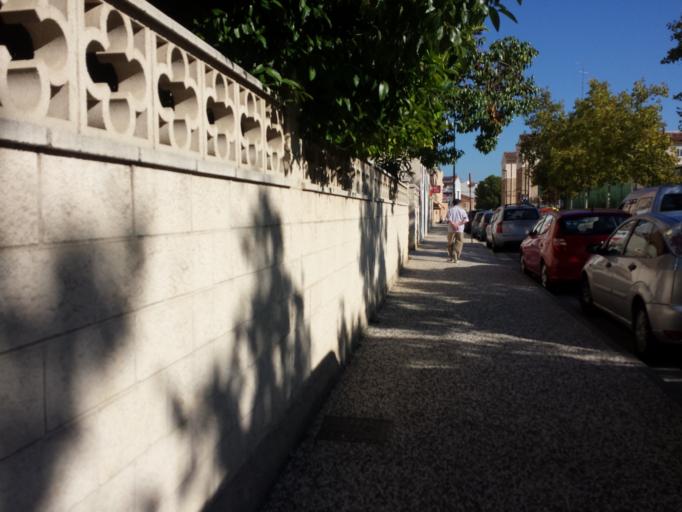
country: ES
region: Aragon
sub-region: Provincia de Zaragoza
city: Oliver-Valdefierro, Oliver, Valdefierro
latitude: 41.6508
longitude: -0.9286
